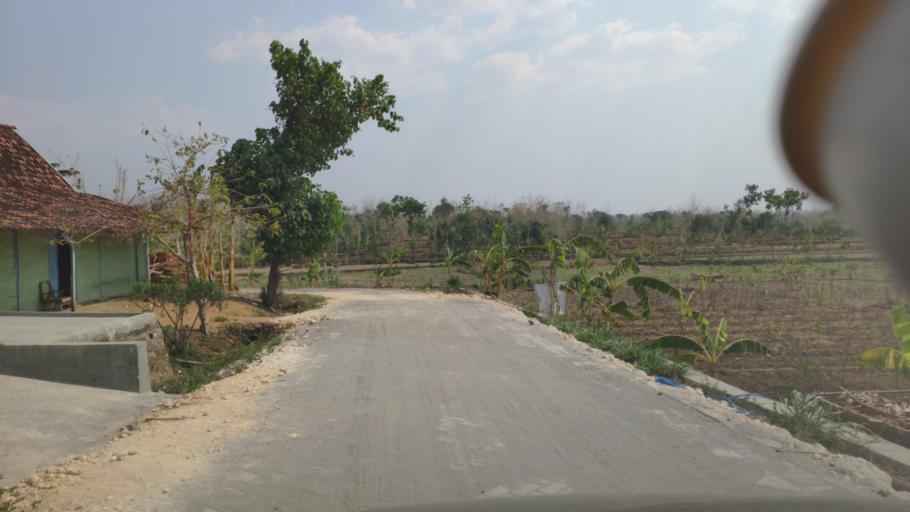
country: ID
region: Central Java
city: Jagong
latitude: -7.0865
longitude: 111.2246
